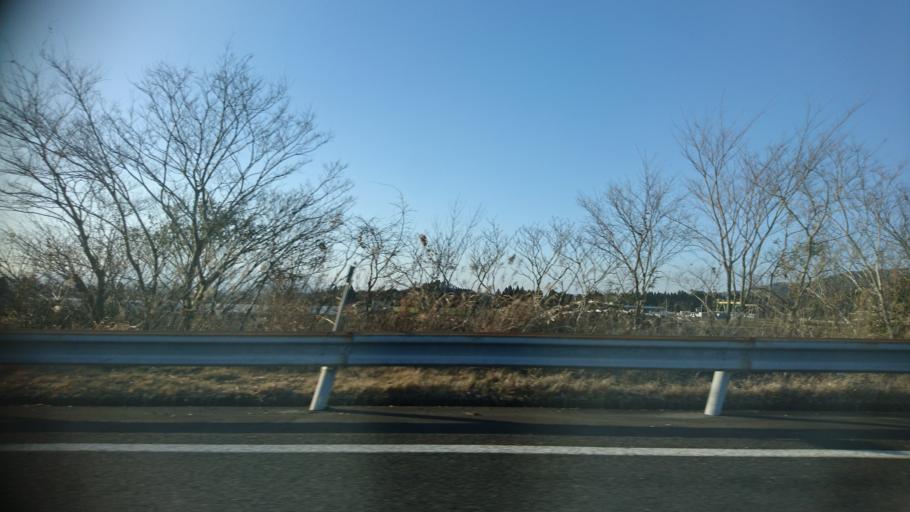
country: JP
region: Miyazaki
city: Miyakonojo
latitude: 31.7897
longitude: 131.1524
